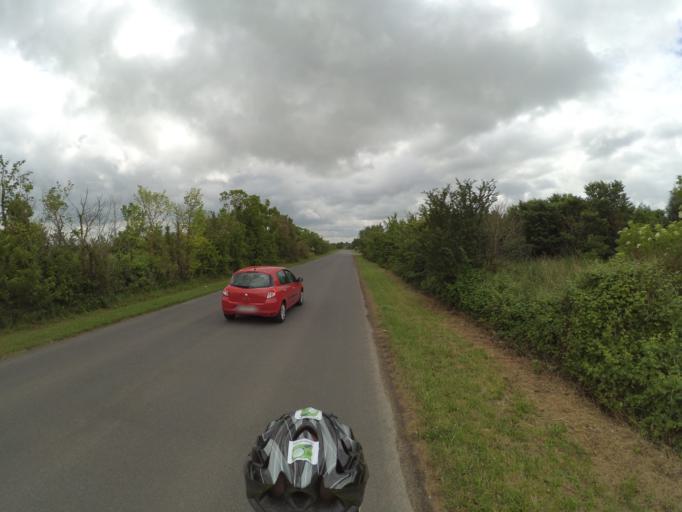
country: FR
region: Poitou-Charentes
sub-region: Departement de la Charente-Maritime
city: Saint-Laurent-de-la-Pree
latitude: 45.9813
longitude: -1.0008
